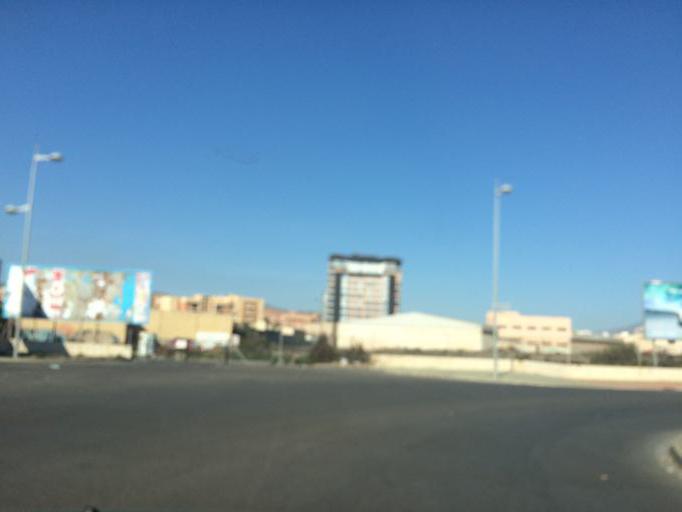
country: ES
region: Andalusia
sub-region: Provincia de Almeria
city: Almeria
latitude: 36.8389
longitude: -2.4396
